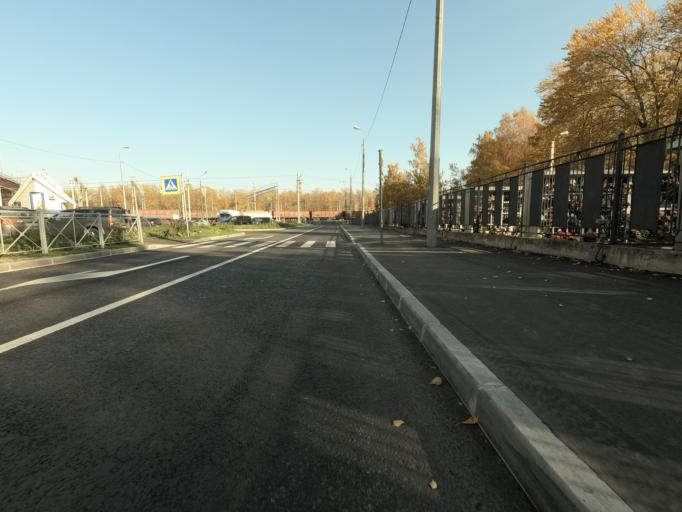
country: RU
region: St.-Petersburg
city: Obukhovo
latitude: 59.8536
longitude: 30.4453
